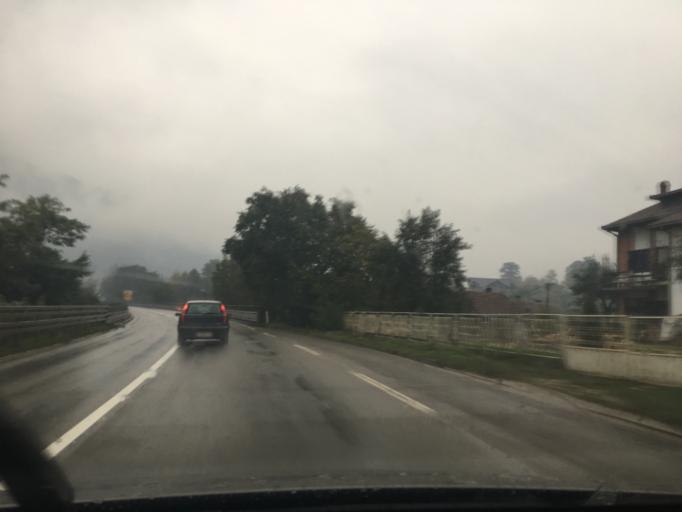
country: RS
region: Central Serbia
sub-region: Pcinjski Okrug
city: Vladicin Han
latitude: 42.8280
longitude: 22.1317
